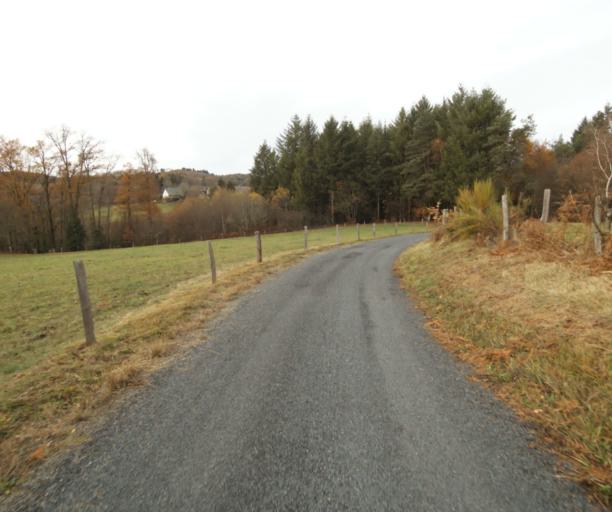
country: FR
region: Limousin
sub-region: Departement de la Correze
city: Sainte-Fortunade
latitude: 45.1792
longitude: 1.7856
